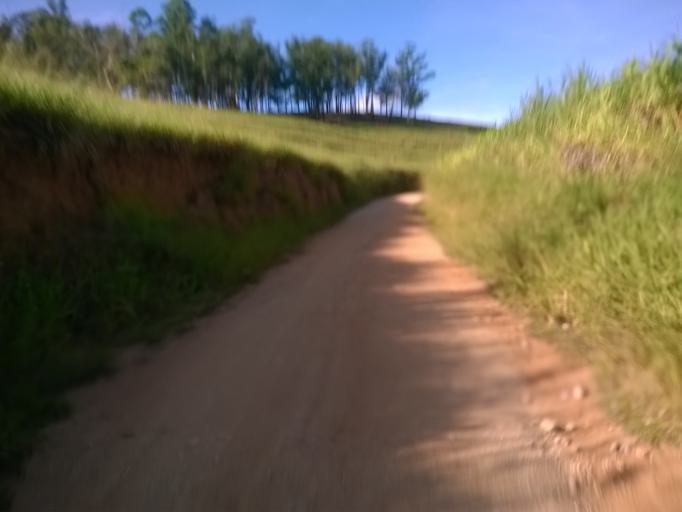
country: BR
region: Minas Gerais
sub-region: Uba
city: Uba
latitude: -21.0869
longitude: -43.0059
